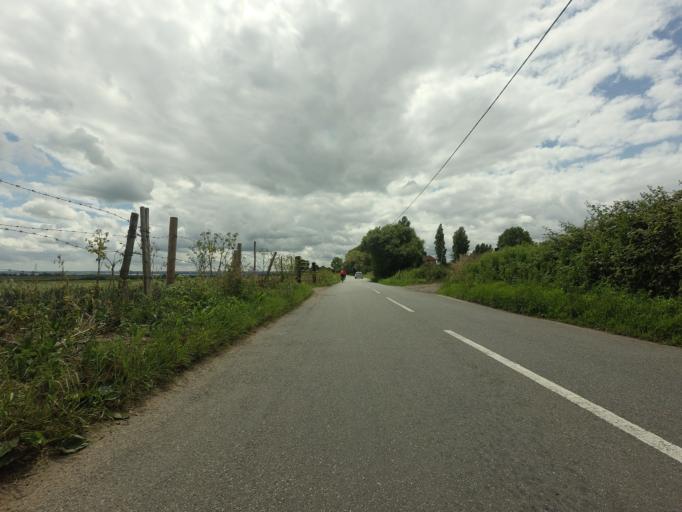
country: GB
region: England
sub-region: Medway
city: Allhallows
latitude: 51.4652
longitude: 0.6406
